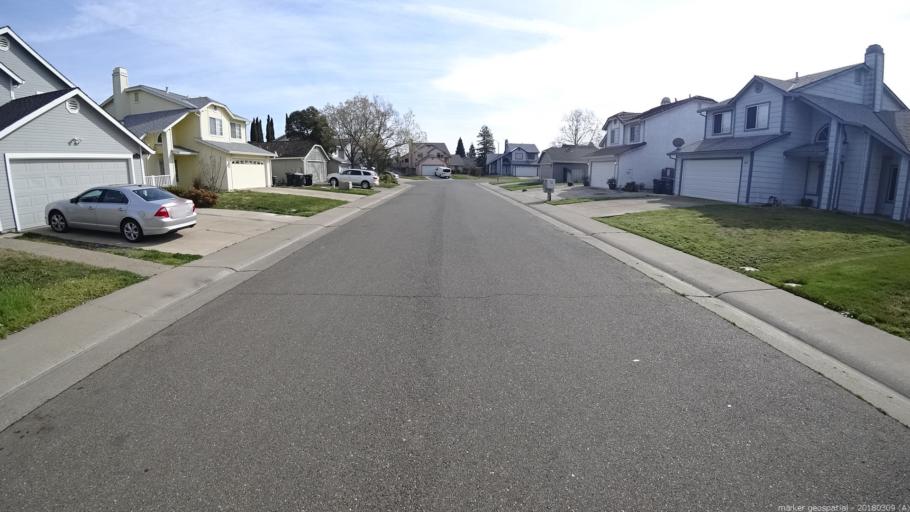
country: US
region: California
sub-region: Sacramento County
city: Florin
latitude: 38.4593
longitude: -121.4007
